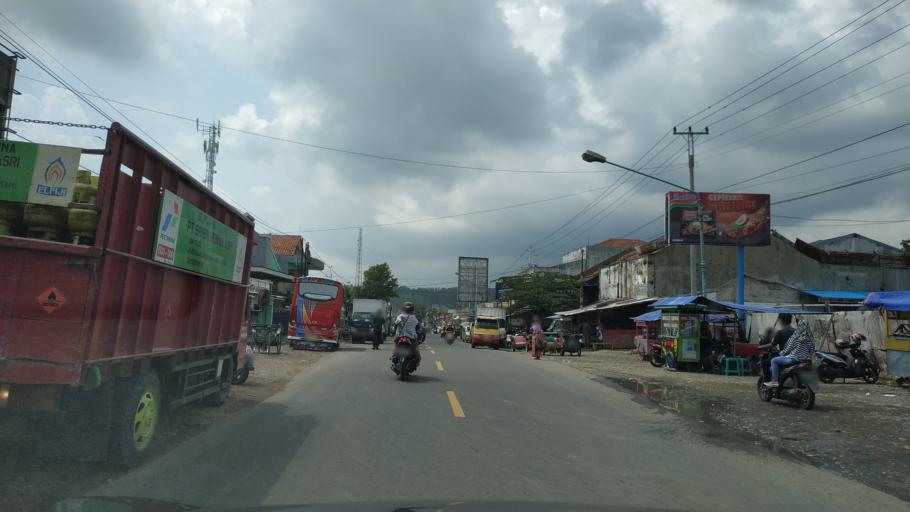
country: ID
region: Central Java
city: Lebaksiu
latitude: -7.0464
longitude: 109.1412
